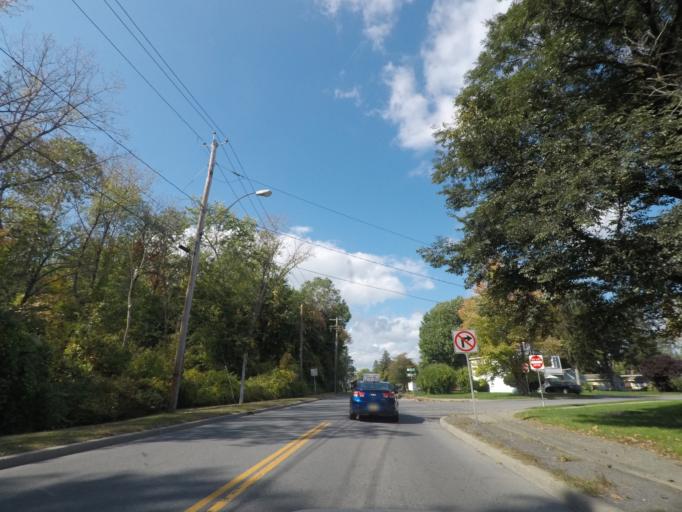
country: US
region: New York
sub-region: Albany County
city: Roessleville
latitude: 42.6600
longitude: -73.8164
